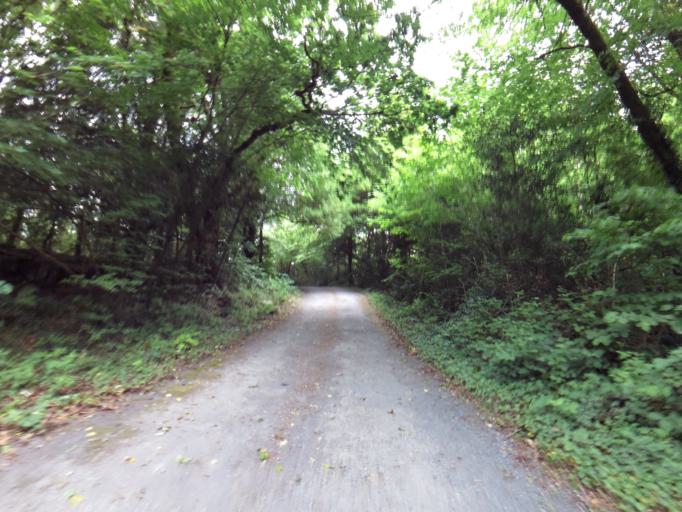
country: IE
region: Connaught
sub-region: County Galway
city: Gort
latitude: 53.0791
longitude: -8.8672
